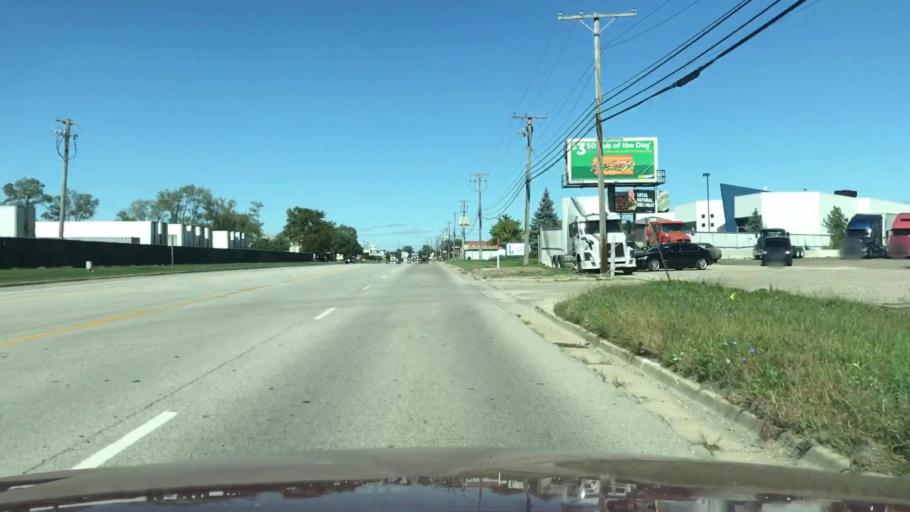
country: US
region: Illinois
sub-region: Cook County
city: Elk Grove Village
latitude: 42.0183
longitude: -87.9535
